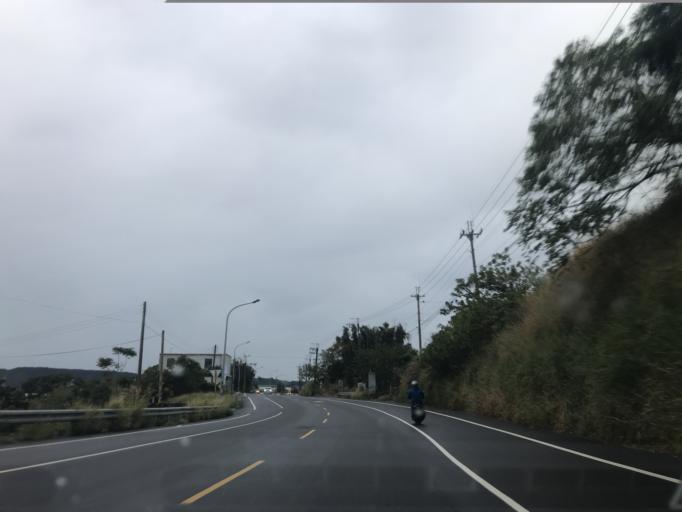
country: TW
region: Taiwan
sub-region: Hsinchu
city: Zhubei
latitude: 24.8343
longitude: 121.0935
